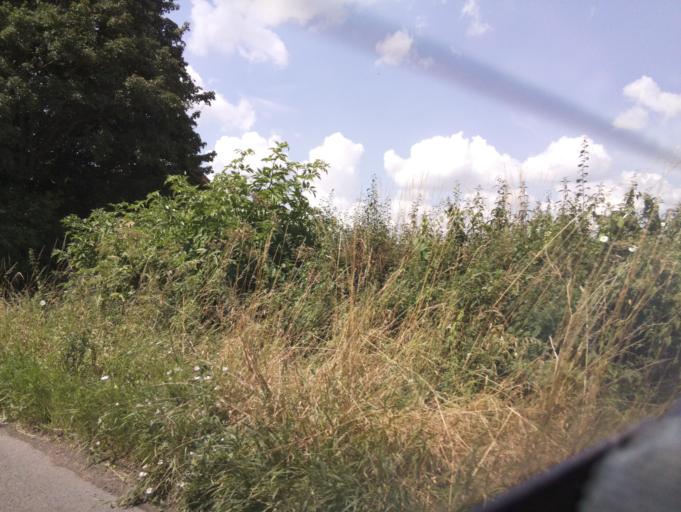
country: GB
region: England
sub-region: Wiltshire
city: Purton
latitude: 51.5745
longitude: -1.8618
